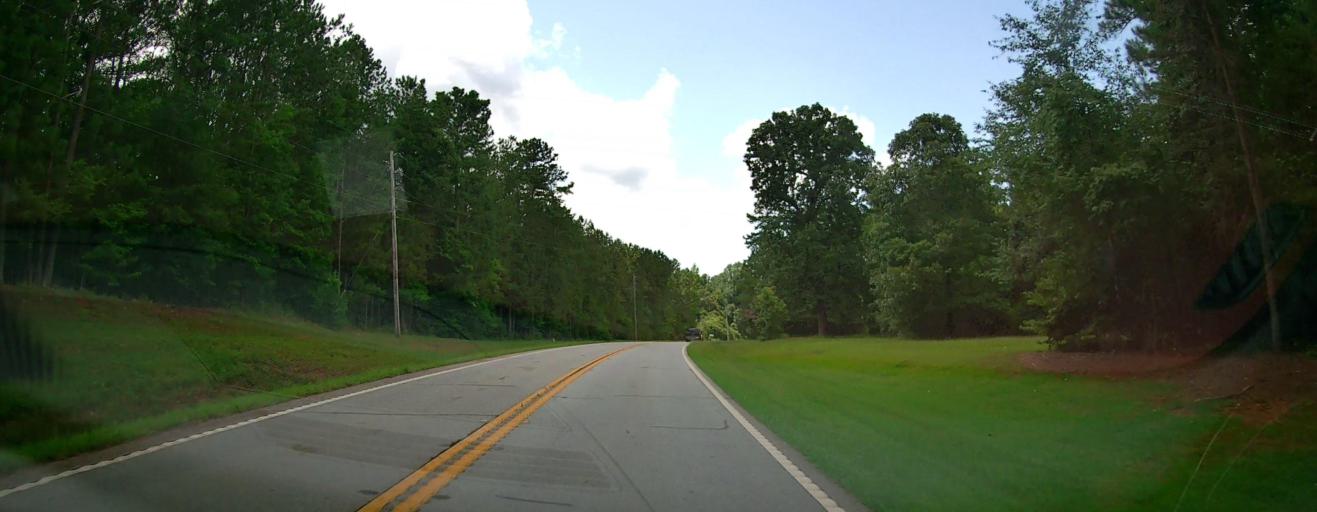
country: US
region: Georgia
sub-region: Heard County
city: Franklin
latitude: 33.3162
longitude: -85.1531
